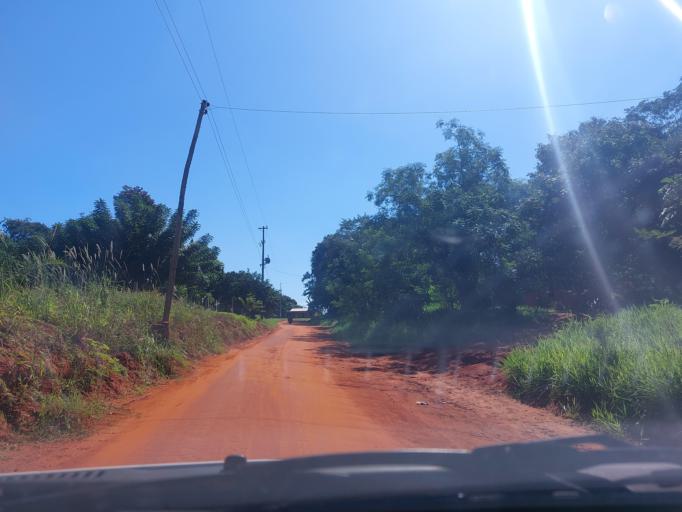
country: PY
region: San Pedro
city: Lima
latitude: -24.1635
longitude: -56.0134
